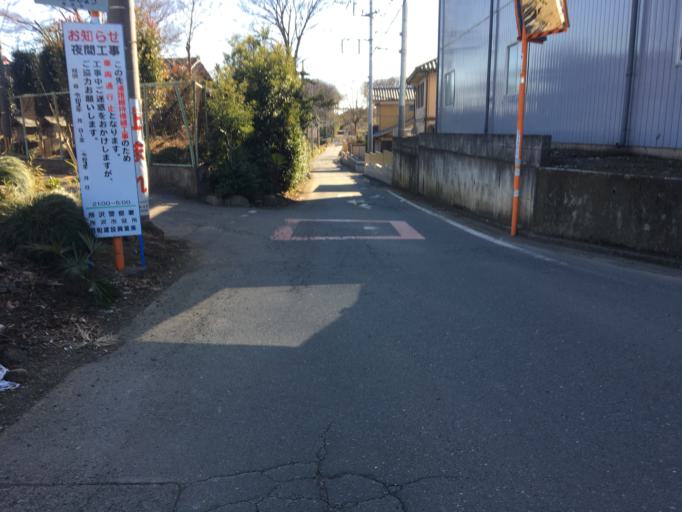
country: JP
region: Saitama
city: Oi
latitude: 35.8164
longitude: 139.5327
